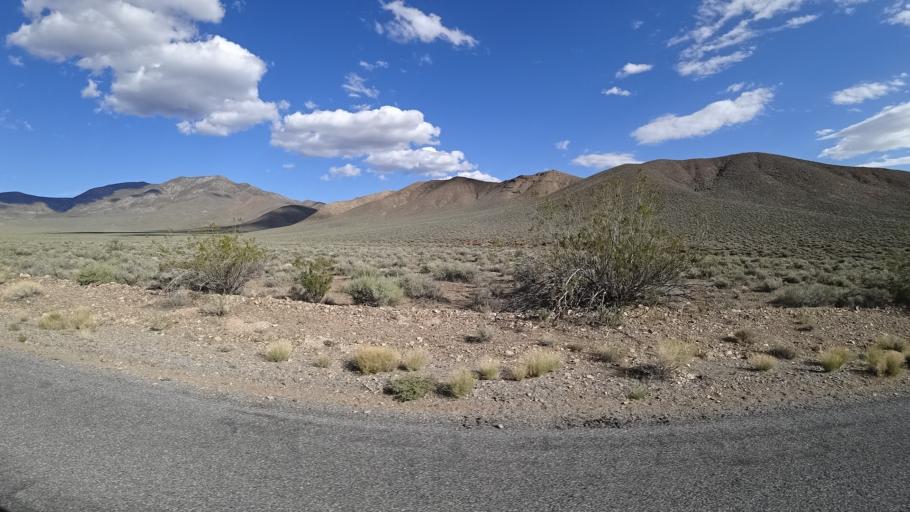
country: US
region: California
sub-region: San Bernardino County
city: Searles Valley
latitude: 36.3021
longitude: -117.1658
